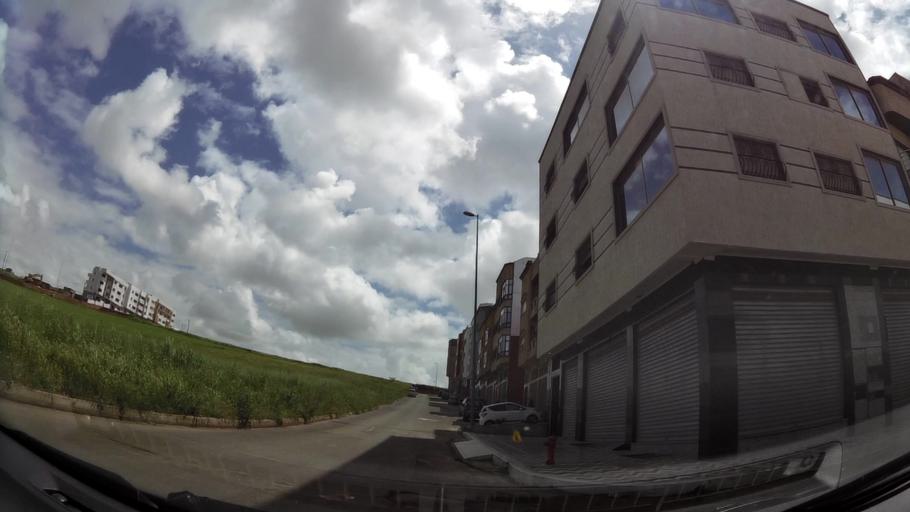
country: MA
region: Grand Casablanca
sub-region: Casablanca
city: Casablanca
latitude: 33.5265
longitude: -7.6008
